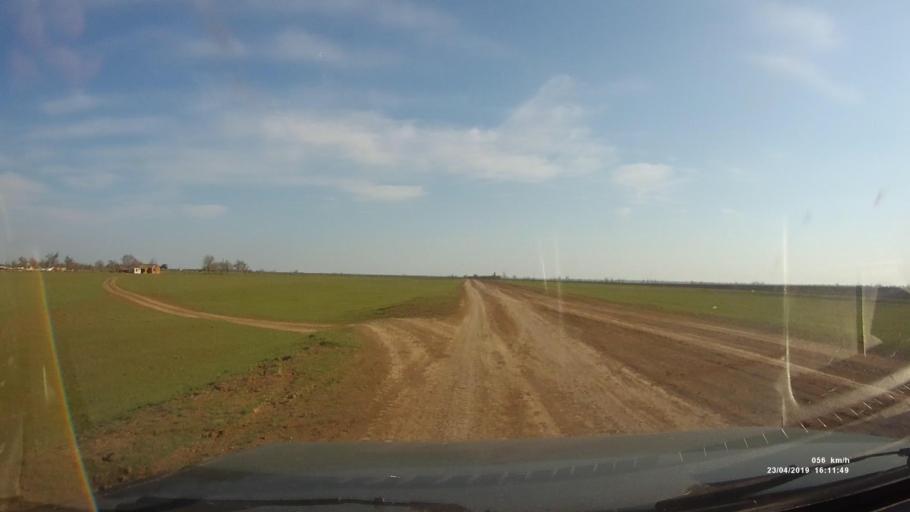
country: RU
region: Kalmykiya
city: Priyutnoye
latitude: 46.4688
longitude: 43.1232
